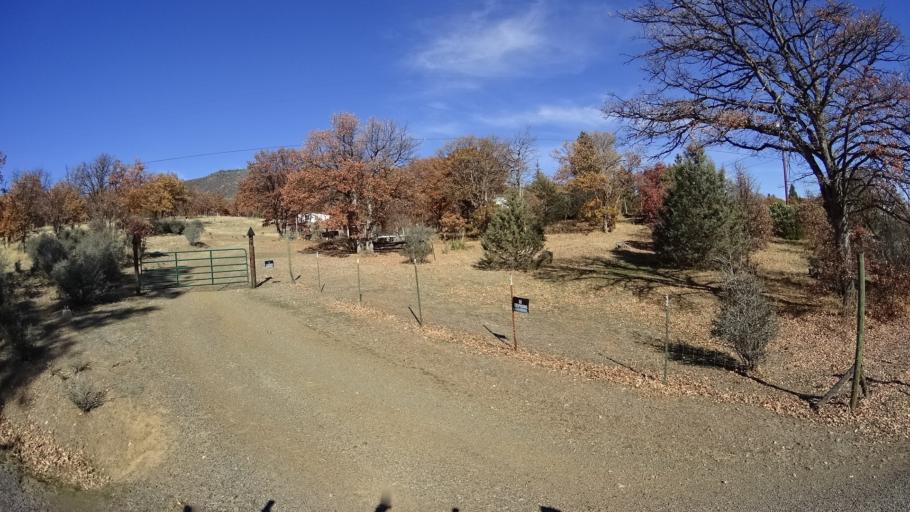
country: US
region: California
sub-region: Siskiyou County
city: Yreka
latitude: 41.7712
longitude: -122.6409
